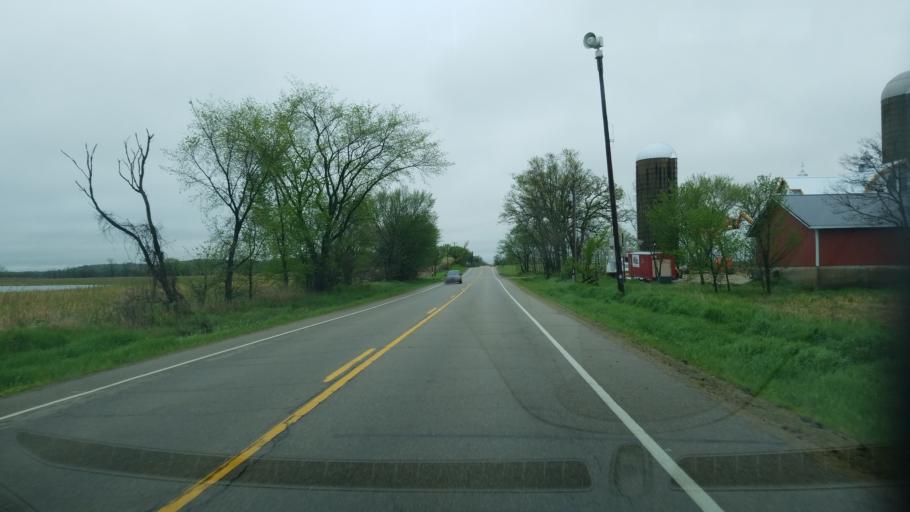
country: US
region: Wisconsin
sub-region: Dane County
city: Fitchburg
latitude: 42.9593
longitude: -89.4372
